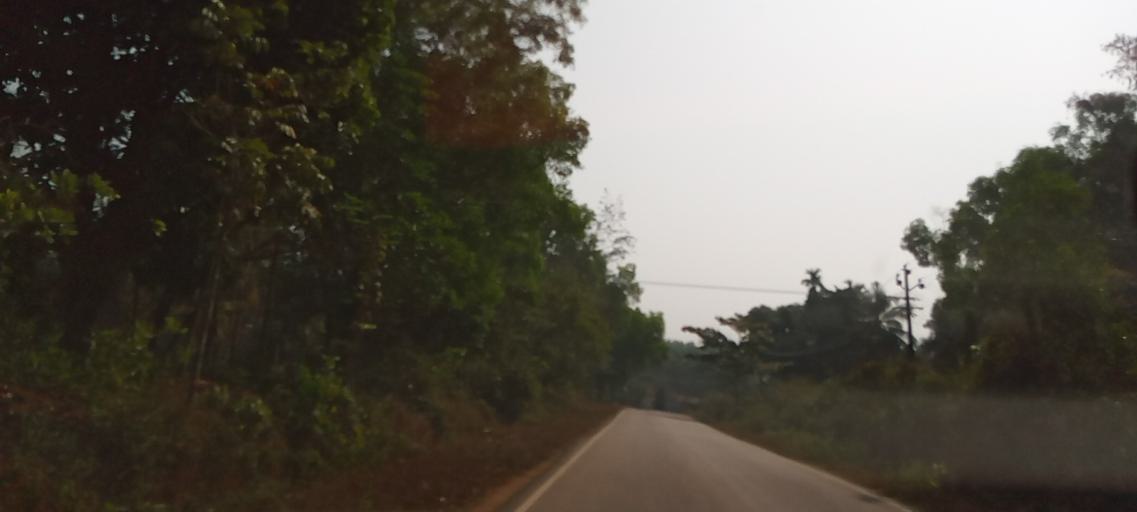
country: IN
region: Karnataka
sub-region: Udupi
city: Manipala
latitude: 13.5114
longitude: 74.8146
